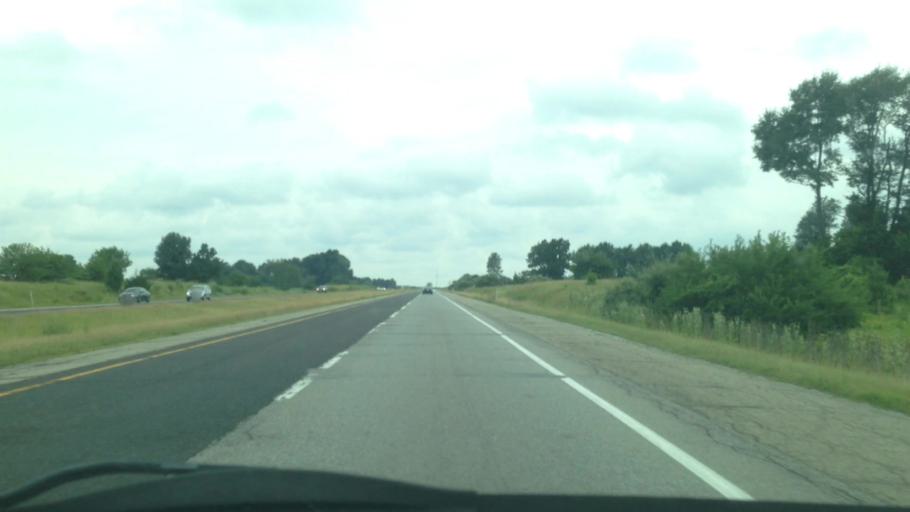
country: US
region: Indiana
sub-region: Steuben County
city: Angola
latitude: 41.7472
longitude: -85.0667
